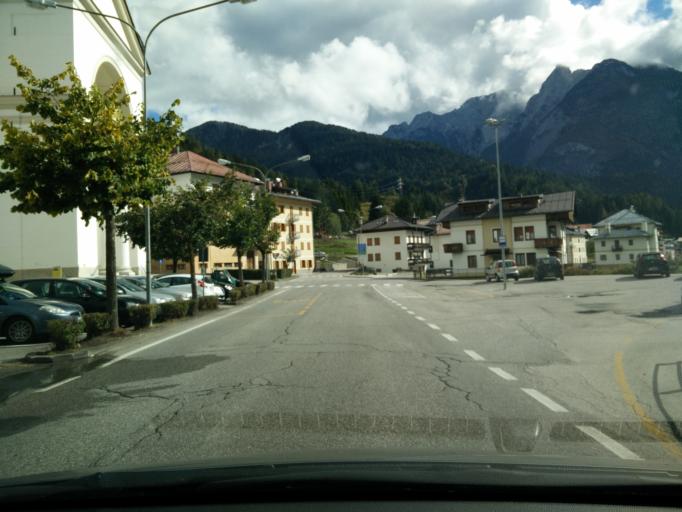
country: IT
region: Veneto
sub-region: Provincia di Belluno
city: Auronzo
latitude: 46.5454
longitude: 12.4572
